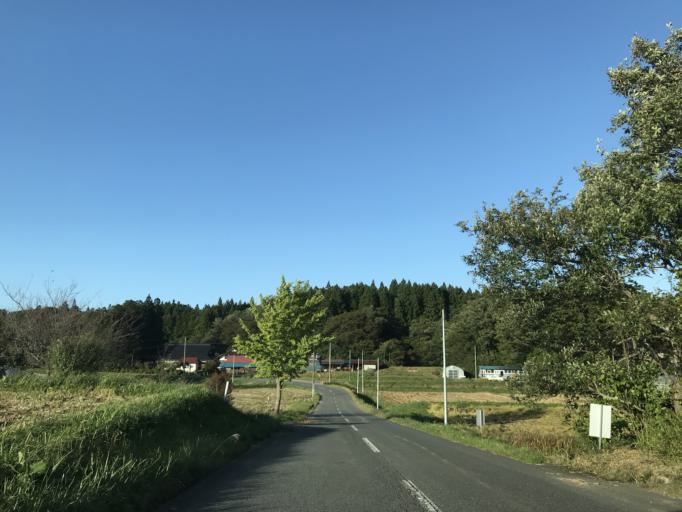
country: JP
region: Iwate
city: Ichinoseki
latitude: 38.9286
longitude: 141.0446
